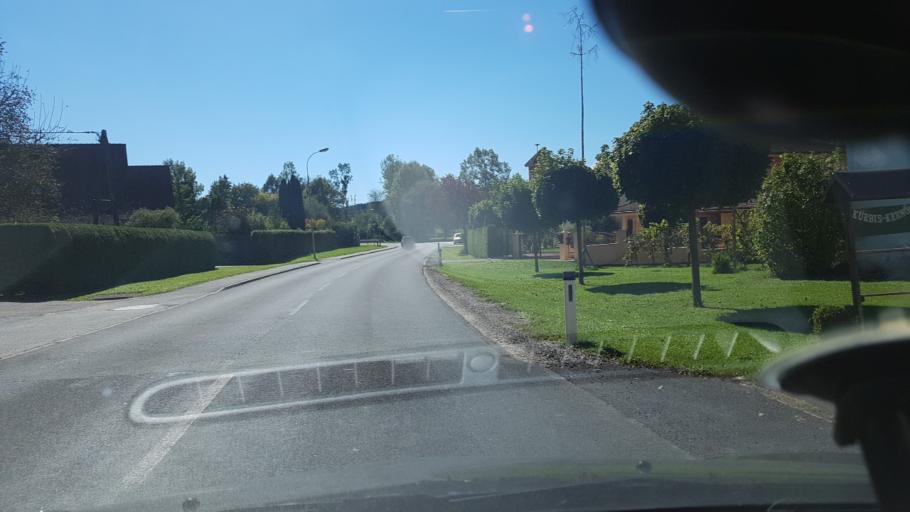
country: AT
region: Styria
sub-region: Politischer Bezirk Weiz
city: Sinabelkirchen
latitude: 47.1246
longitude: 15.8115
